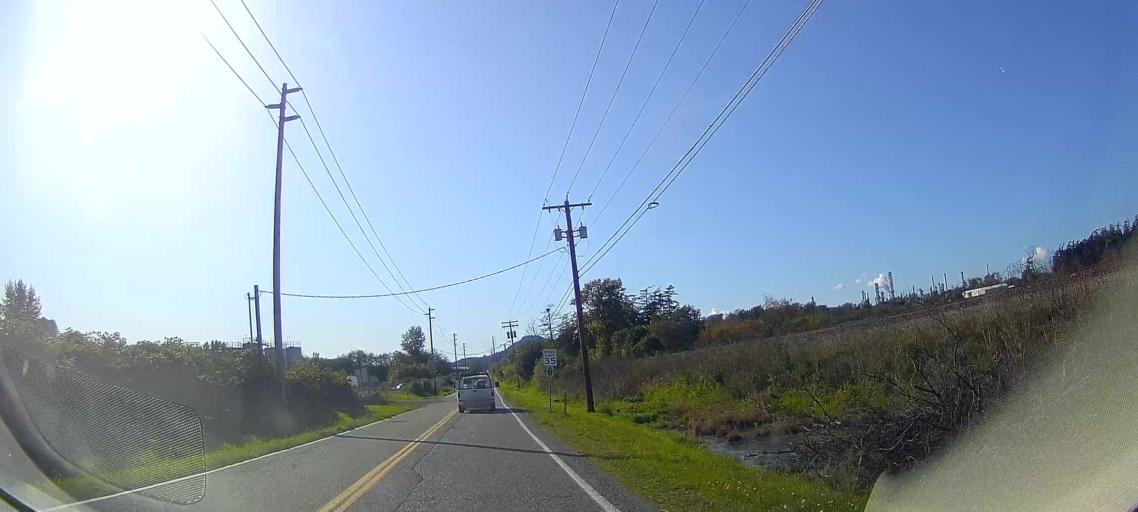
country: US
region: Washington
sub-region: Skagit County
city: Anacortes
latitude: 48.4654
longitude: -122.5377
